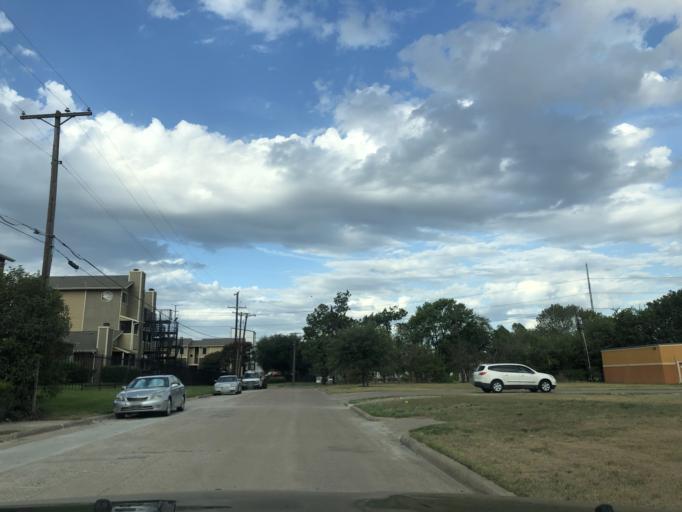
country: US
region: Texas
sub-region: Dallas County
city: Garland
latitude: 32.8773
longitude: -96.6579
